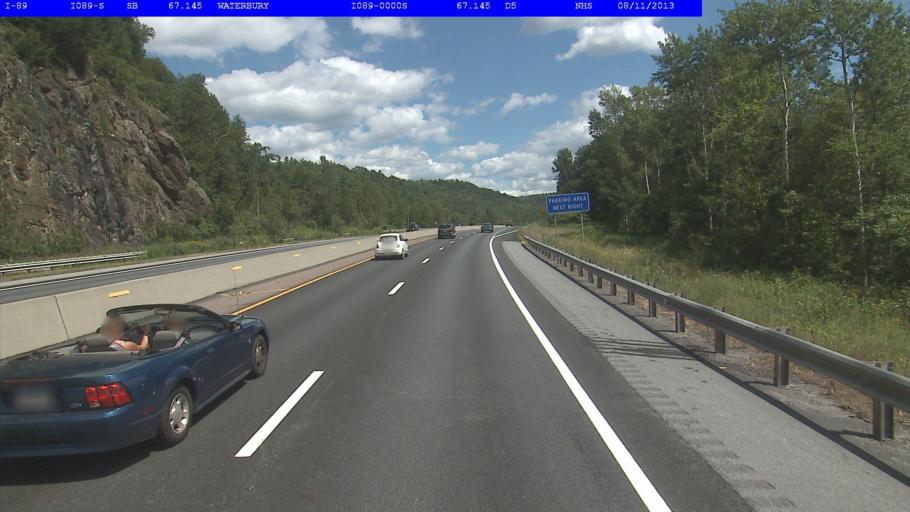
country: US
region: Vermont
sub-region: Washington County
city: Waterbury
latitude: 44.3612
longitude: -72.8134
